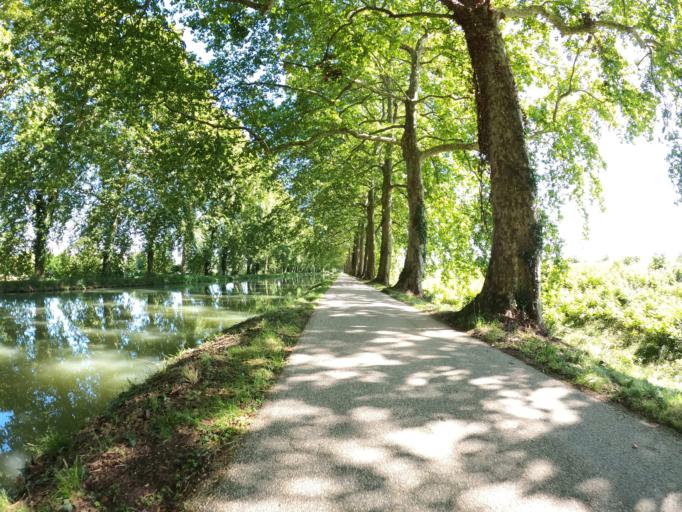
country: FR
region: Midi-Pyrenees
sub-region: Departement du Tarn-et-Garonne
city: Auvillar
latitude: 44.0948
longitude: 0.9449
